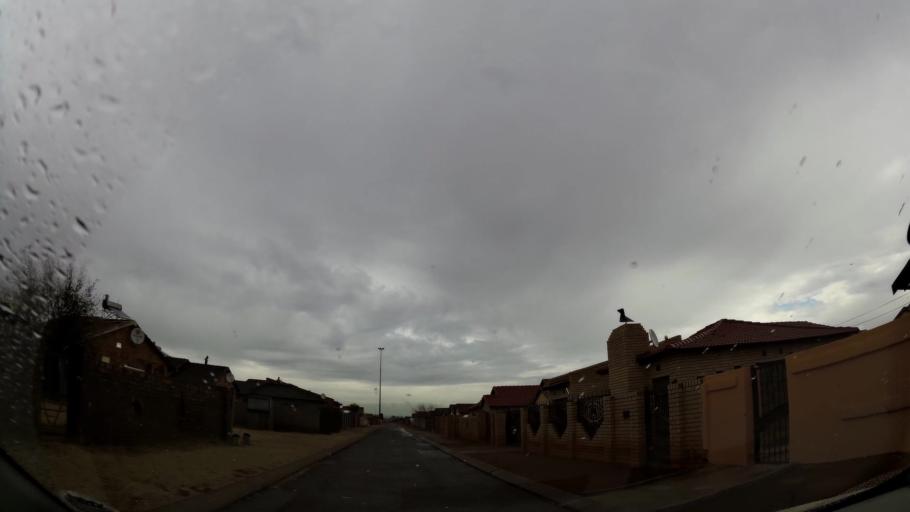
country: ZA
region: Gauteng
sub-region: Ekurhuleni Metropolitan Municipality
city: Germiston
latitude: -26.3347
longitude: 28.2020
